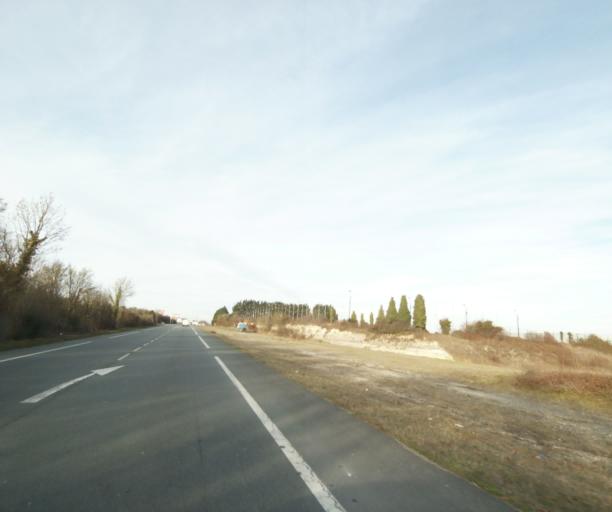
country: FR
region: Poitou-Charentes
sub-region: Departement de la Charente-Maritime
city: Saintes
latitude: 45.7415
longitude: -0.6609
